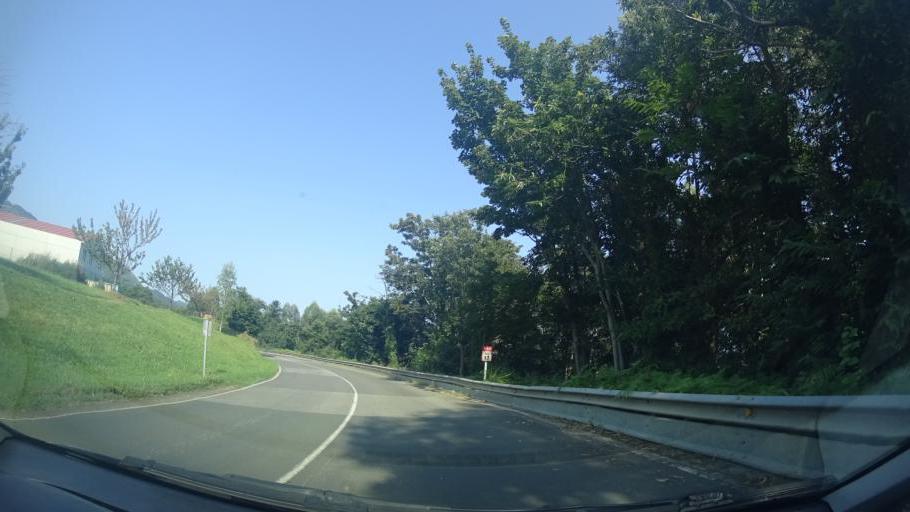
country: ES
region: Asturias
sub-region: Province of Asturias
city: Colunga
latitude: 43.4634
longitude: -5.1977
